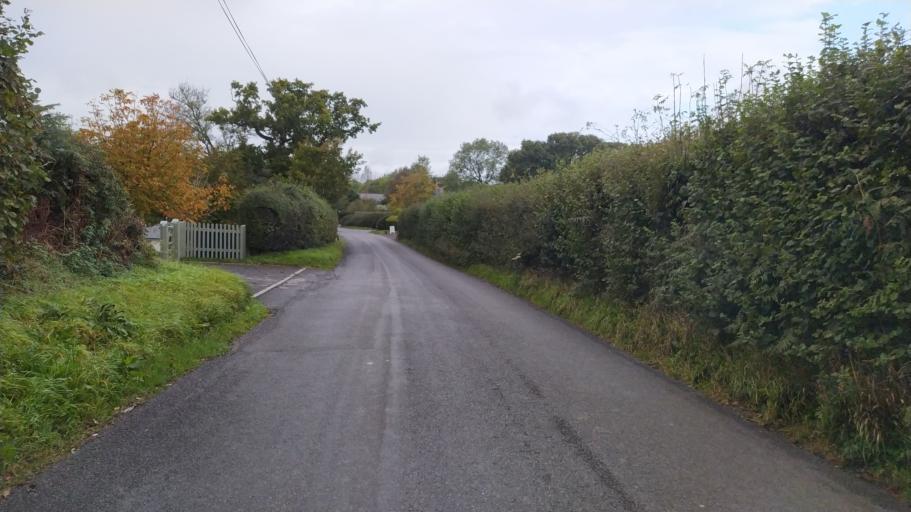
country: GB
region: England
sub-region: Dorset
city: Shaftesbury
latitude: 51.0413
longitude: -2.1919
